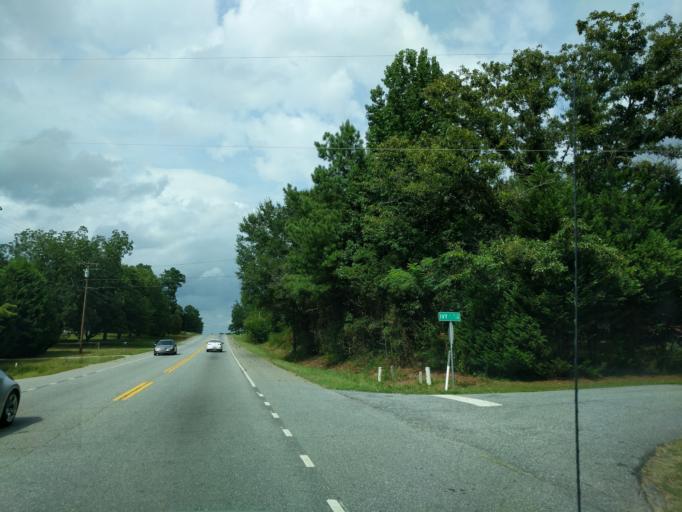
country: US
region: South Carolina
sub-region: Anderson County
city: Anderson
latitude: 34.5334
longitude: -82.5845
